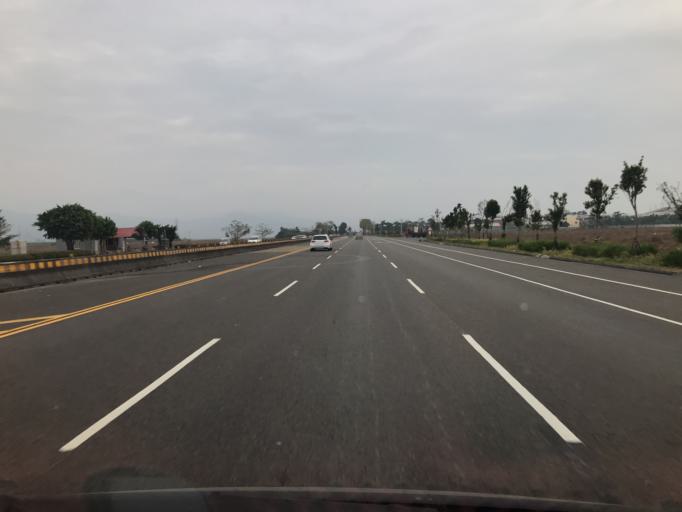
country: TW
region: Taiwan
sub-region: Pingtung
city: Pingtung
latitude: 22.4237
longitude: 120.5799
